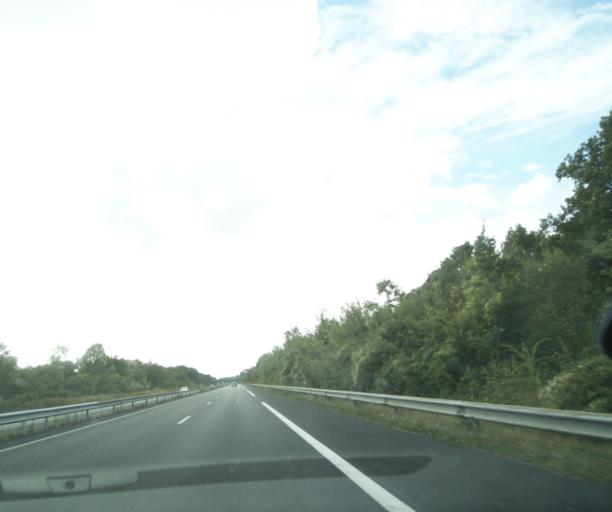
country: FR
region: Poitou-Charentes
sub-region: Departement de la Charente-Maritime
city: Thenac
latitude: 45.6605
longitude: -0.6358
